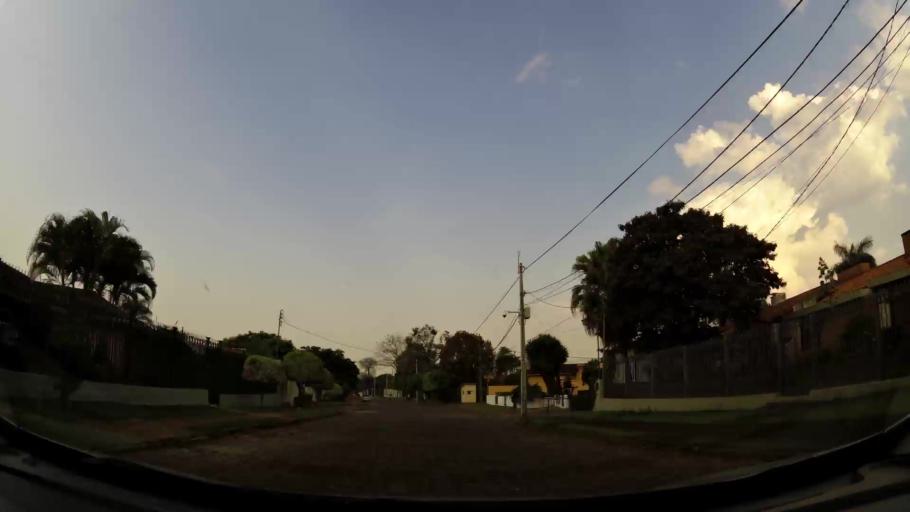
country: PY
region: Alto Parana
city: Presidente Franco
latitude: -25.5172
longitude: -54.6395
